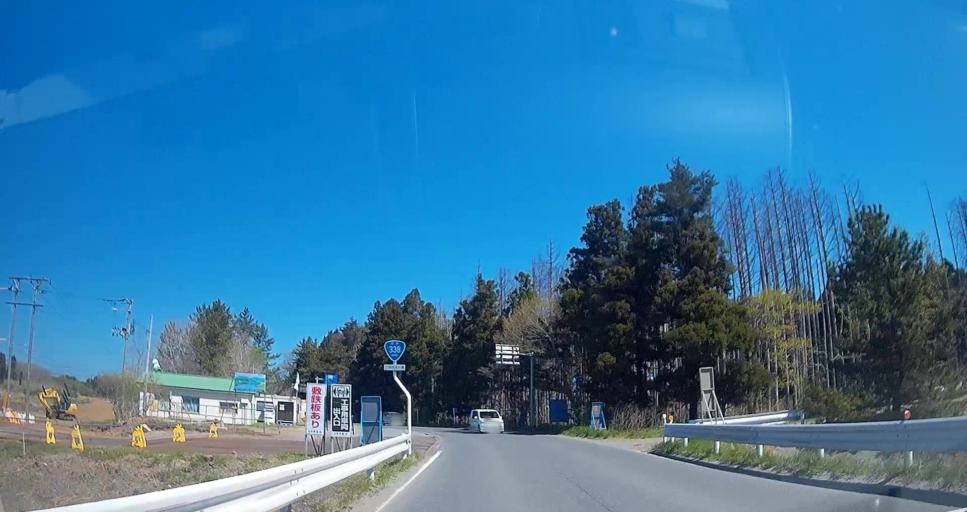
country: JP
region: Aomori
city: Misawa
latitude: 40.8446
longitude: 141.3833
